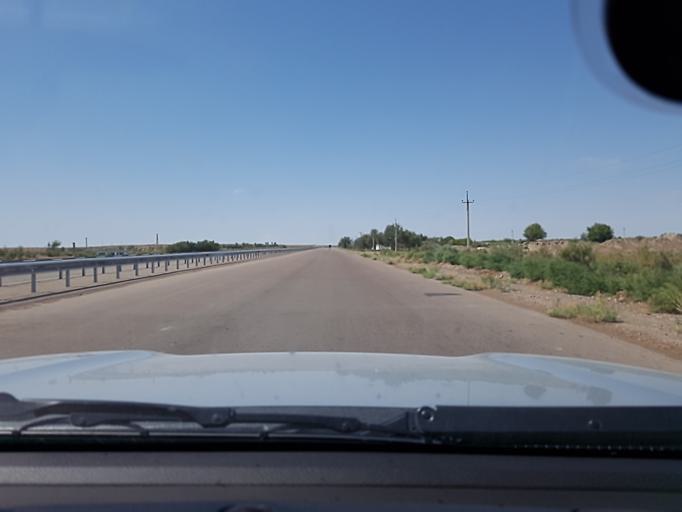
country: TM
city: Akdepe
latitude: 41.7503
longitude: 59.3232
